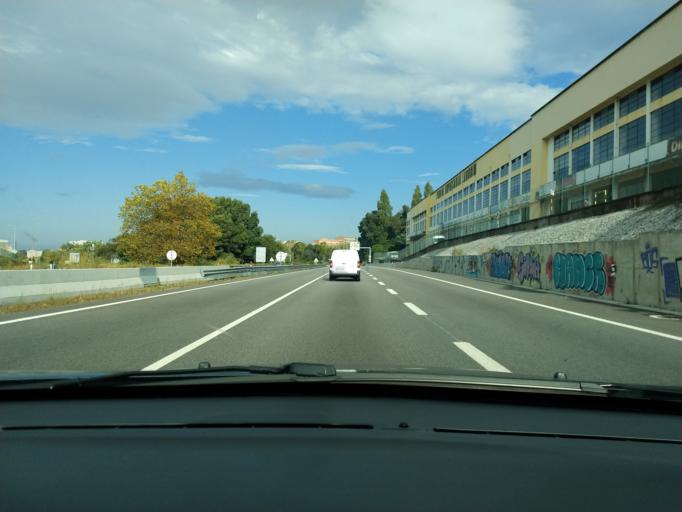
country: PT
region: Porto
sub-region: Vila Nova de Gaia
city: Vilar de Andorinho
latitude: 41.1065
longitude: -8.6039
